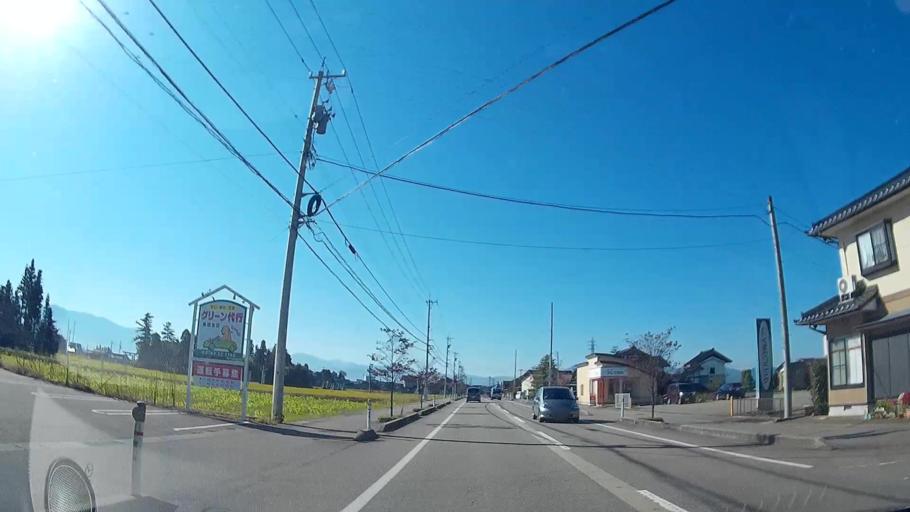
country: JP
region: Toyama
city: Nanto-shi
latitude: 36.6007
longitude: 136.9302
